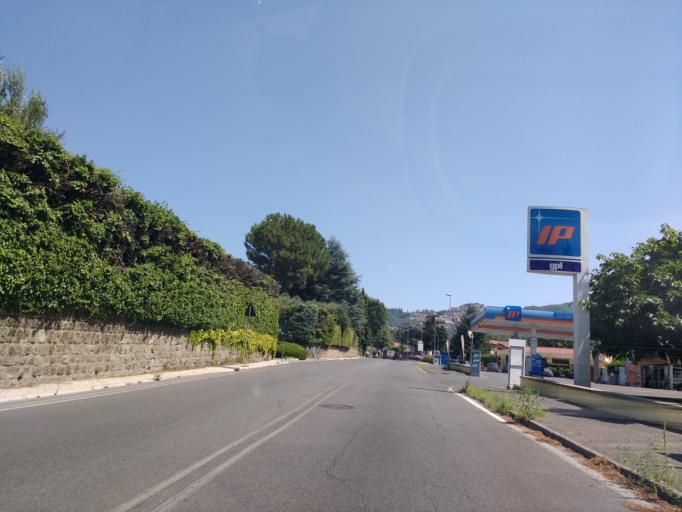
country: IT
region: Latium
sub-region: Citta metropolitana di Roma Capitale
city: Rocca di Papa
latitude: 41.7758
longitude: 12.6895
